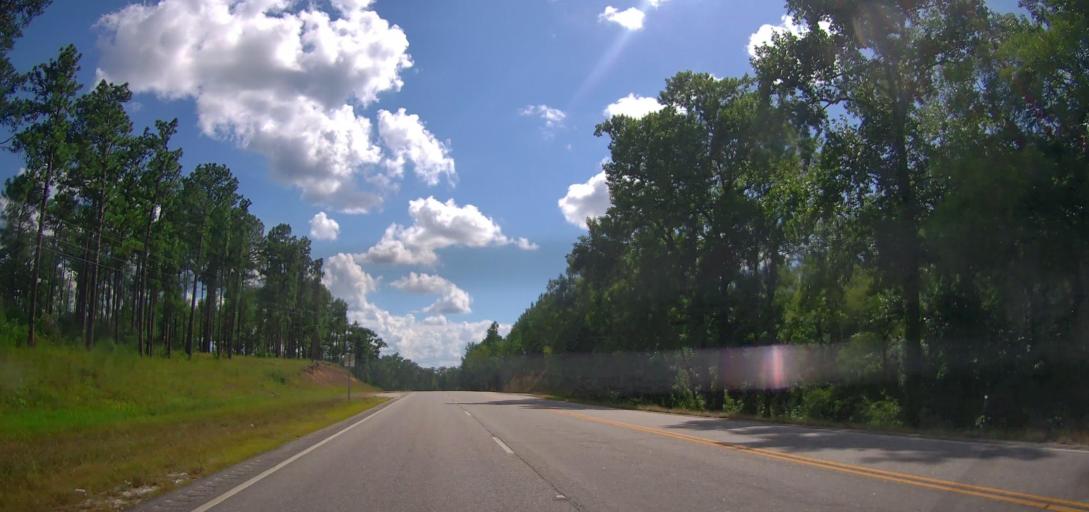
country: US
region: Alabama
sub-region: Macon County
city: Tuskegee
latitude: 32.4518
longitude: -85.6308
